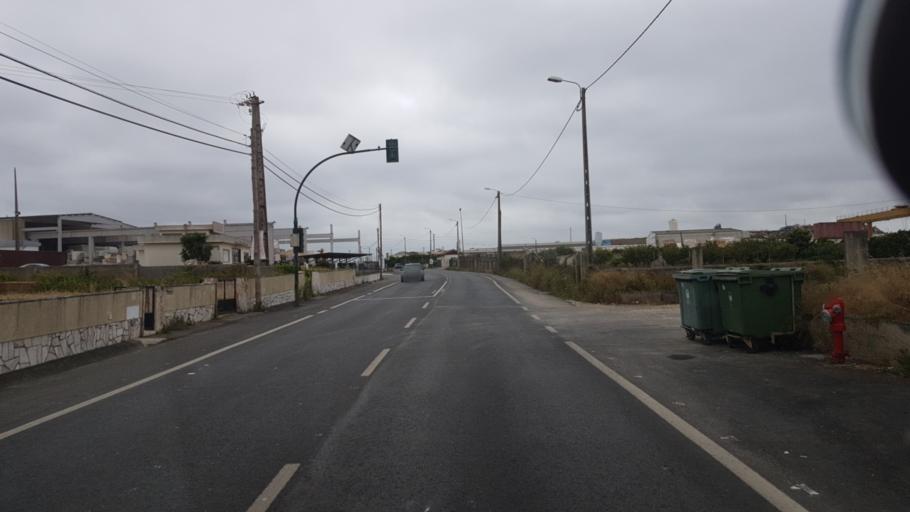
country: PT
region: Lisbon
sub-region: Sintra
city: Pero Pinheiro
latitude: 38.8450
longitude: -9.3362
